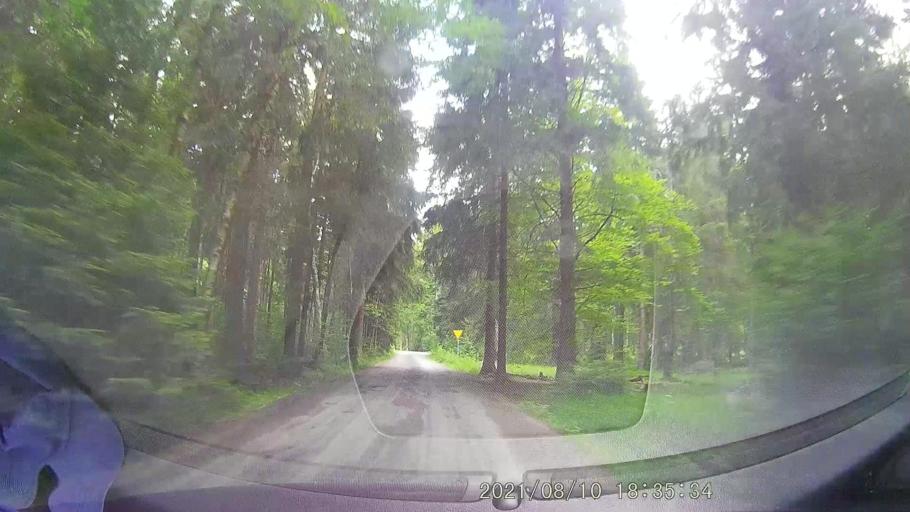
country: PL
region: Lower Silesian Voivodeship
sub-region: Powiat klodzki
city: Radkow
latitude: 50.4774
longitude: 16.3561
